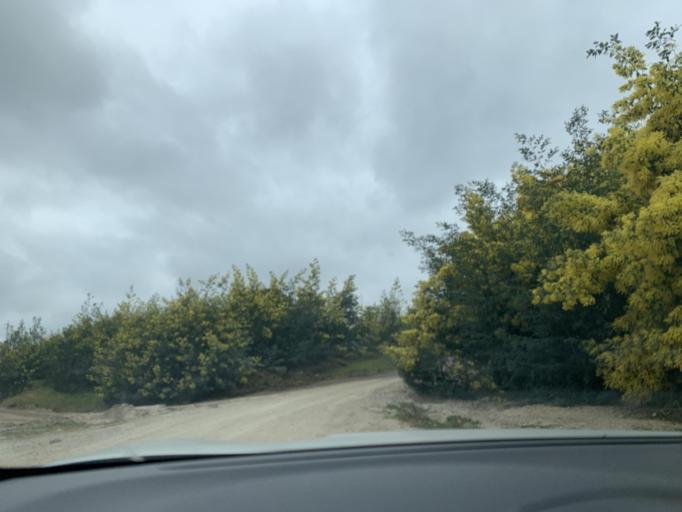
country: PT
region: Viseu
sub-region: Mangualde
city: Mangualde
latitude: 40.6095
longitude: -7.7905
